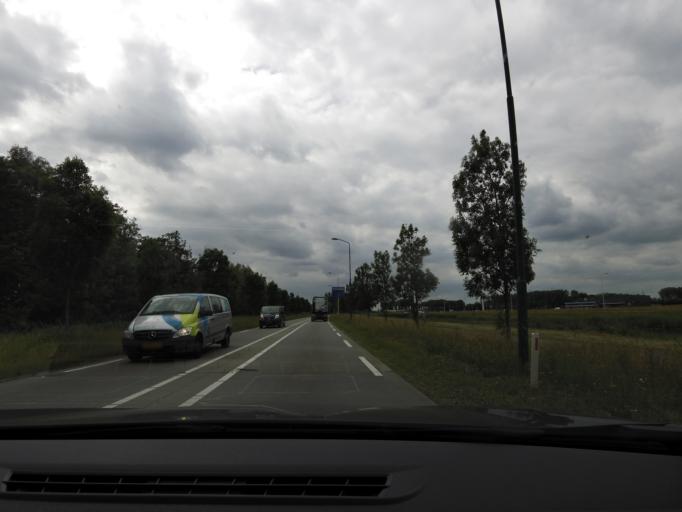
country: NL
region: North Brabant
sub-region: Gemeente Moerdijk
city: Klundert
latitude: 51.6540
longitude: 4.5623
